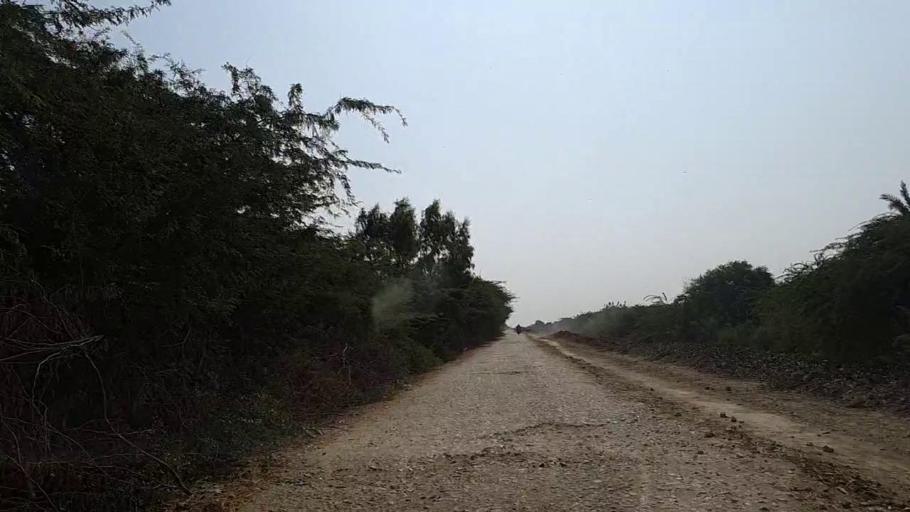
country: PK
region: Sindh
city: Thatta
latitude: 24.7308
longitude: 67.7683
